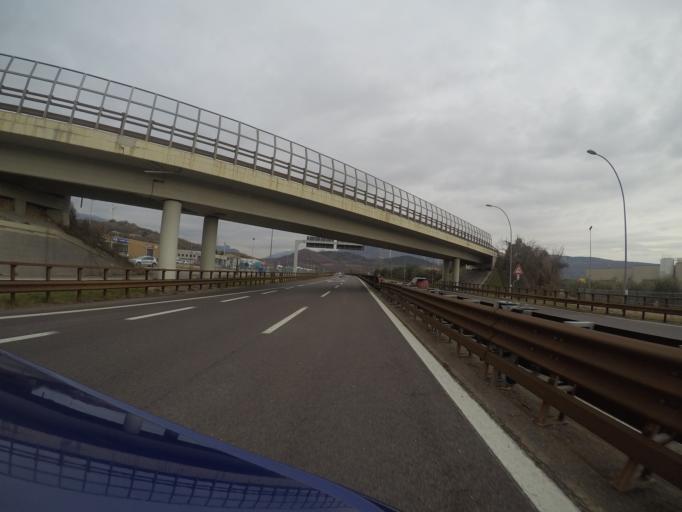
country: IT
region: Veneto
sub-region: Provincia di Verona
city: Affi
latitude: 45.5508
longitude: 10.7939
